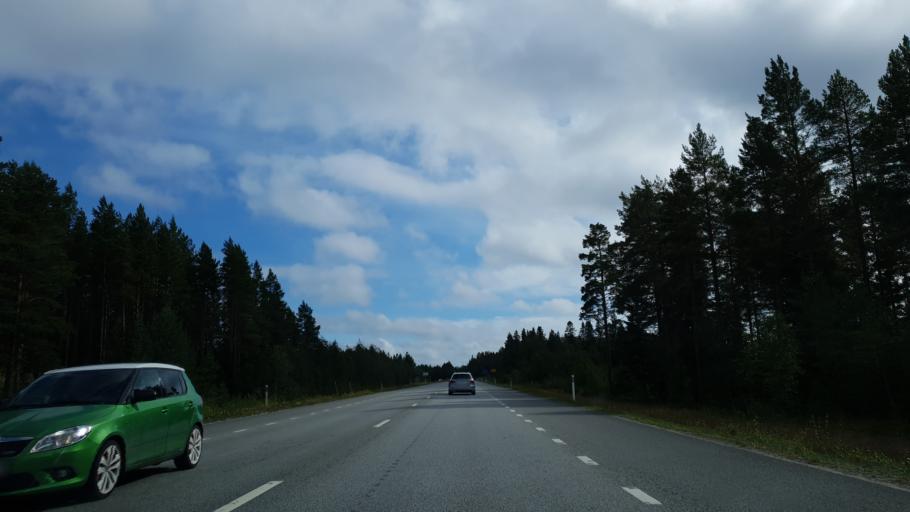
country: SE
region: Vaesterbotten
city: Obbola
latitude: 63.7190
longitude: 20.3004
